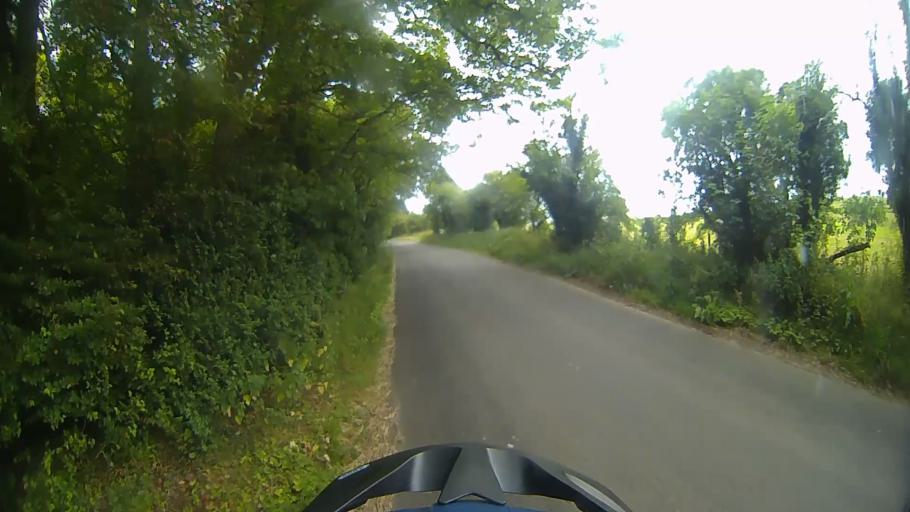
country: GB
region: England
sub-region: Oxfordshire
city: Stanford in the Vale
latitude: 51.5772
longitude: -1.5354
